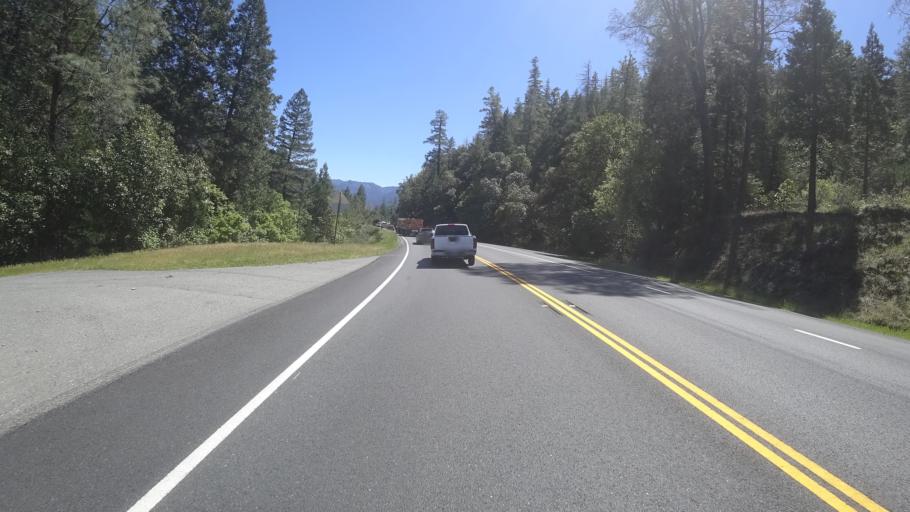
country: US
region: California
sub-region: Humboldt County
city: Willow Creek
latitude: 40.8220
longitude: -123.4834
